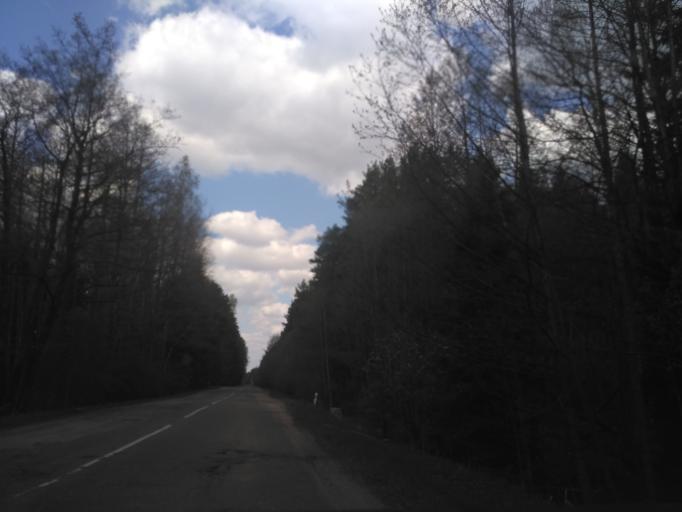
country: BY
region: Minsk
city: Il'ya
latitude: 54.3071
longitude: 27.2634
